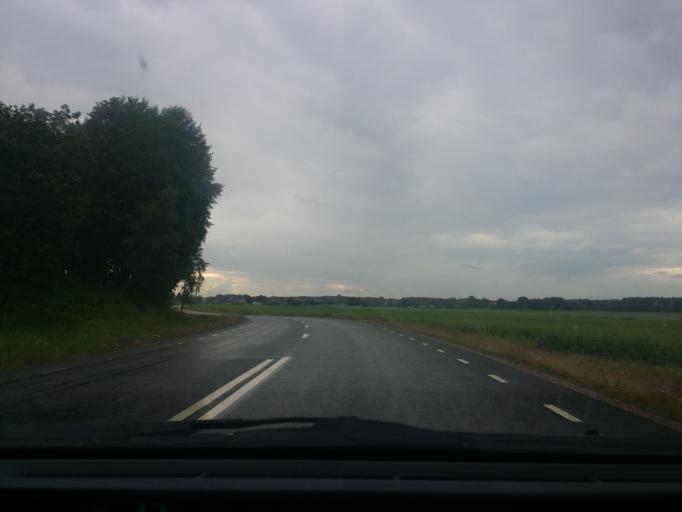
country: SE
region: Vaestmanland
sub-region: Arboga Kommun
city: Arboga
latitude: 59.4028
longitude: 15.8705
